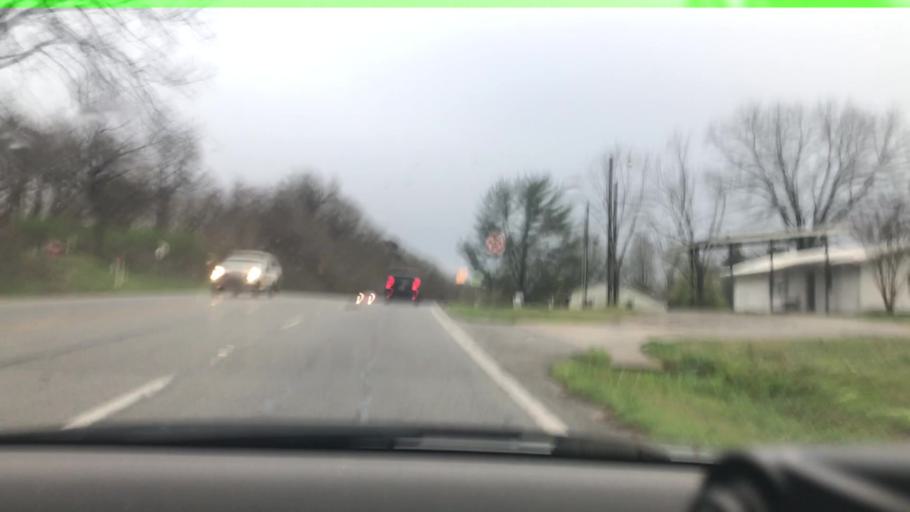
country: US
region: Georgia
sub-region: Oglethorpe County
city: Lexington
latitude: 33.8846
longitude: -83.1662
